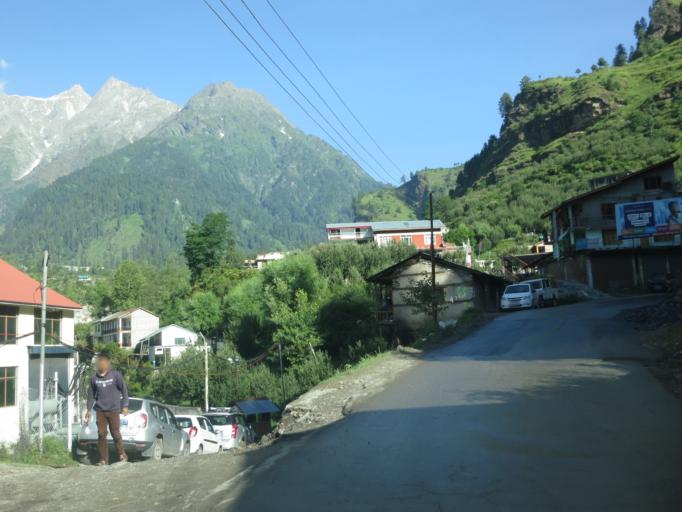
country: IN
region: Himachal Pradesh
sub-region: Kulu
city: Manali
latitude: 32.3092
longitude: 77.1754
